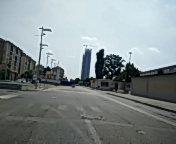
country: IT
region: Piedmont
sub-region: Provincia di Torino
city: Moncalieri
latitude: 45.0321
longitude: 7.6672
